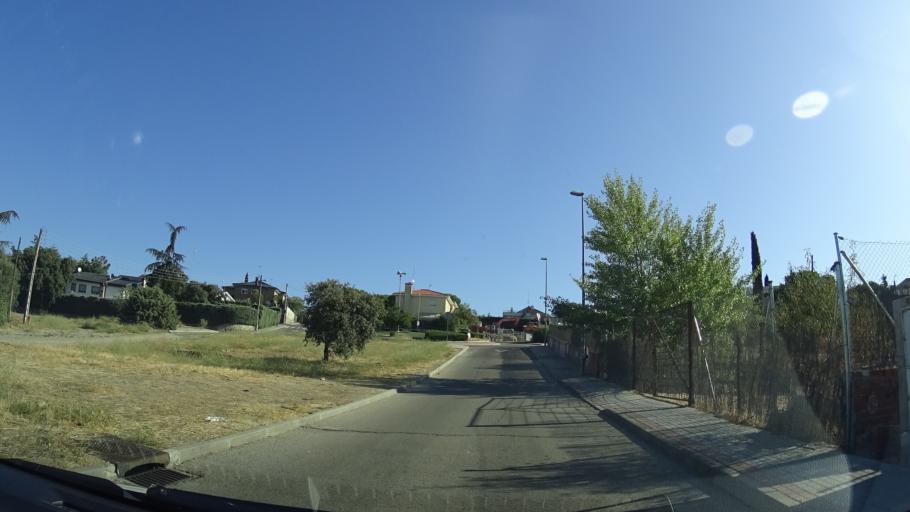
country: ES
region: Madrid
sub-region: Provincia de Madrid
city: Colmenarejo
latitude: 40.5573
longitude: -4.0189
